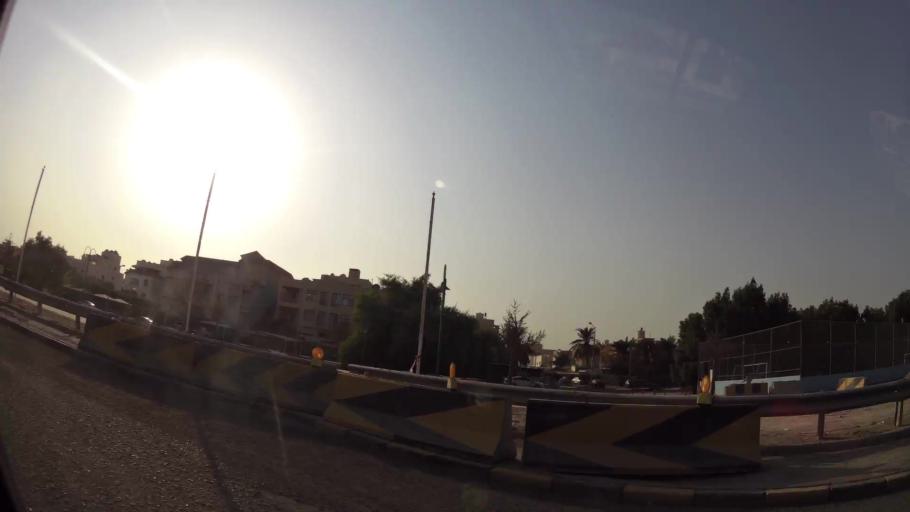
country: KW
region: Muhafazat Hawalli
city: Ar Rumaythiyah
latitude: 29.3183
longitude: 48.0874
